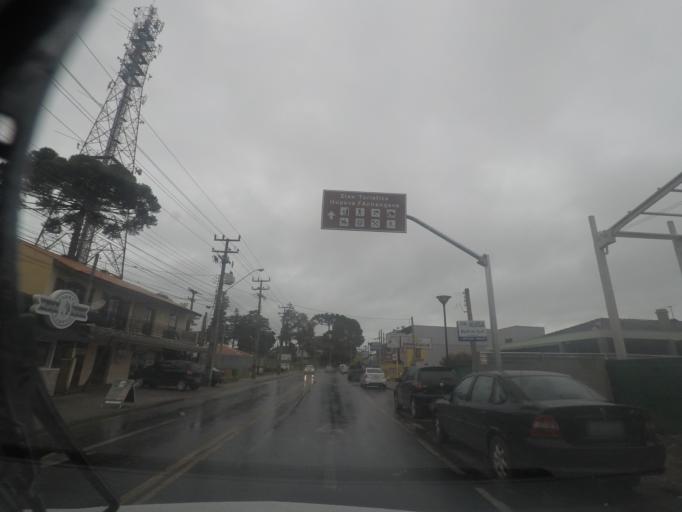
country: BR
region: Parana
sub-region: Quatro Barras
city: Quatro Barras
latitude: -25.3693
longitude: -49.0754
